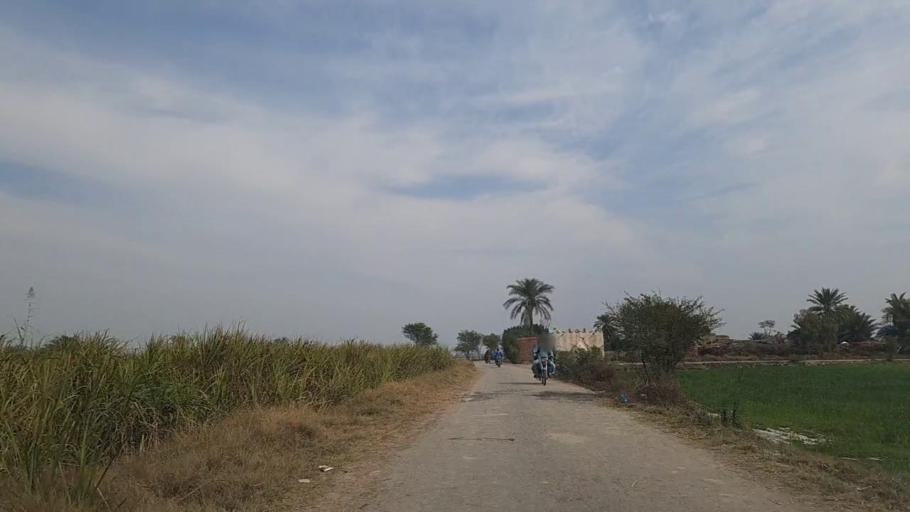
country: PK
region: Sindh
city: Daur
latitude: 26.4976
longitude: 68.3724
